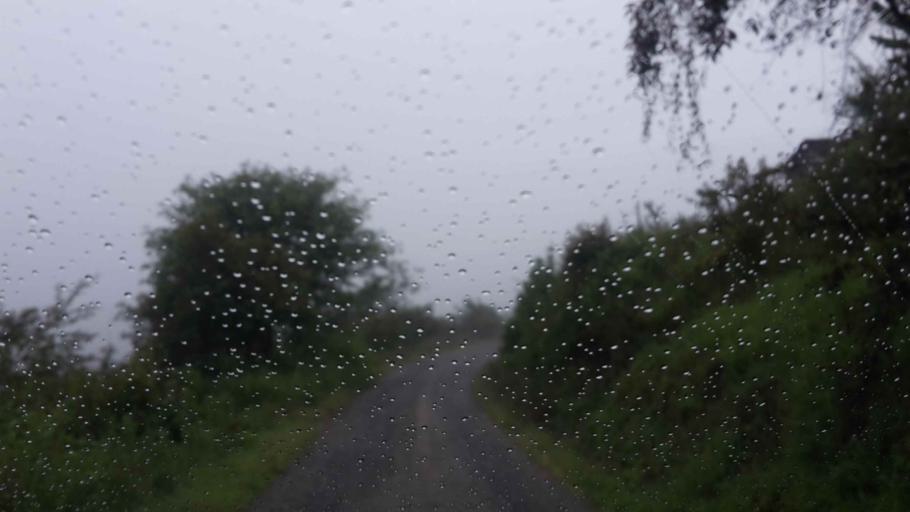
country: BO
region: Cochabamba
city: Colomi
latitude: -17.0833
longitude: -66.0001
